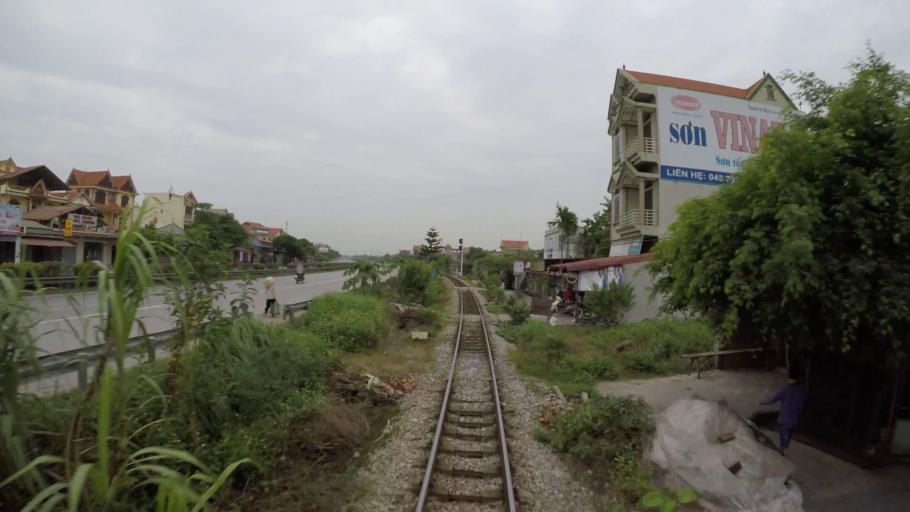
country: VN
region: Hai Duong
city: Phu Thai
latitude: 20.9721
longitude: 106.4409
